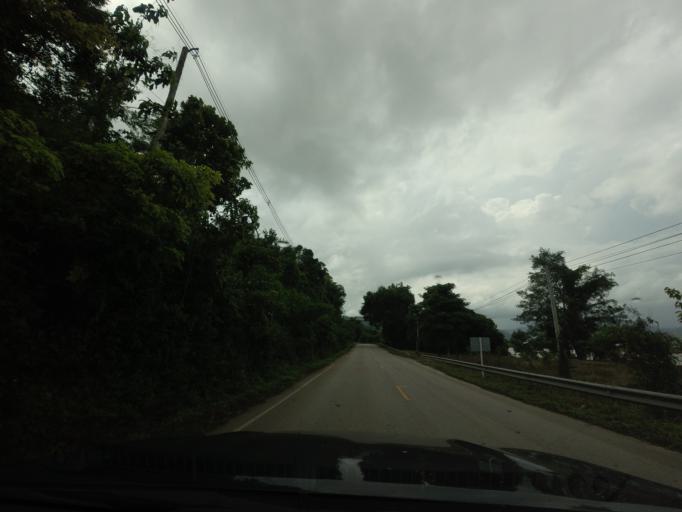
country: TH
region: Loei
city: Pak Chom
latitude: 18.0541
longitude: 101.8214
